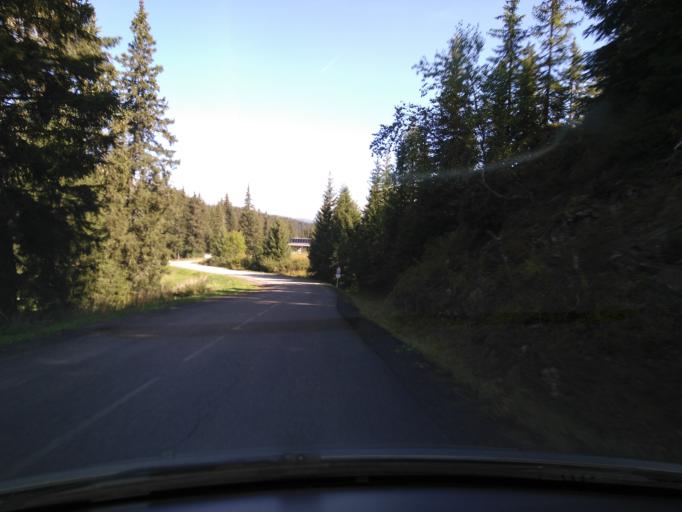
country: FR
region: Rhone-Alpes
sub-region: Departement de la Savoie
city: Beaufort
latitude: 45.7700
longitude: 6.5282
